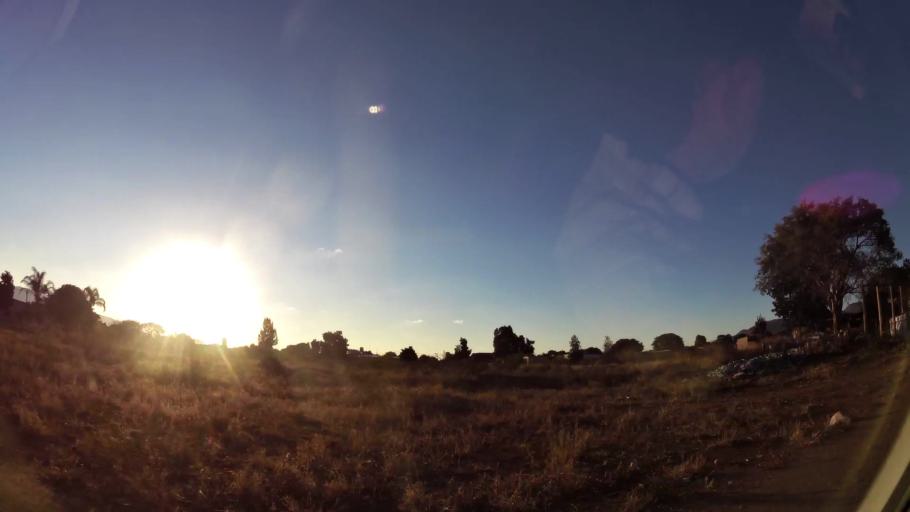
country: ZA
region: Limpopo
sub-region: Waterberg District Municipality
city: Mokopane
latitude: -24.1369
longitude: 28.9971
